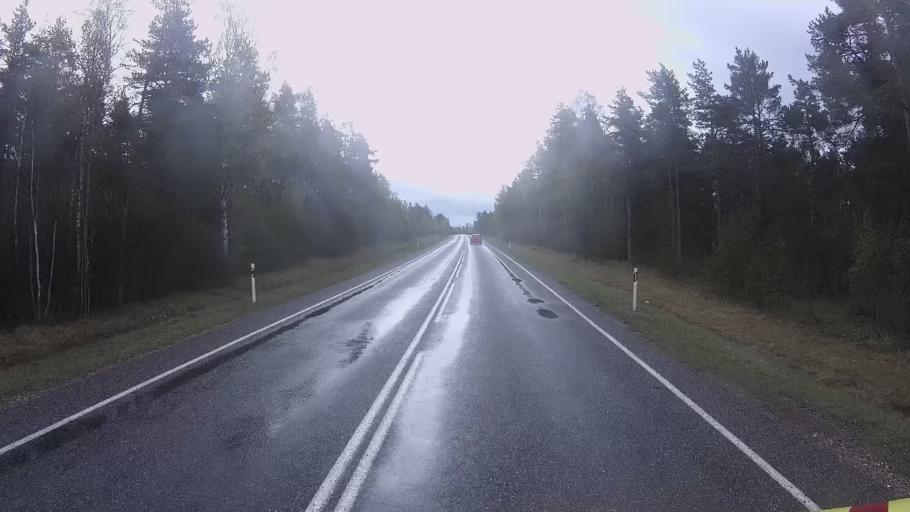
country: EE
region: Hiiumaa
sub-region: Kaerdla linn
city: Kardla
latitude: 58.8825
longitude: 22.9407
